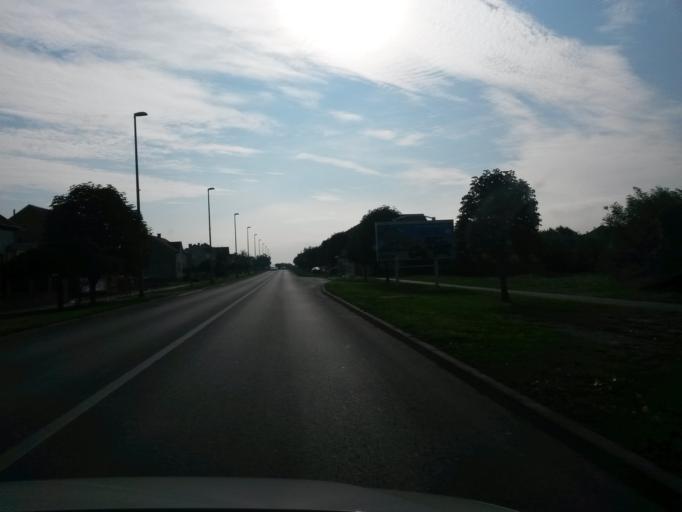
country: HR
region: Vukovarsko-Srijemska
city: Vukovar
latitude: 45.3430
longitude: 19.0130
